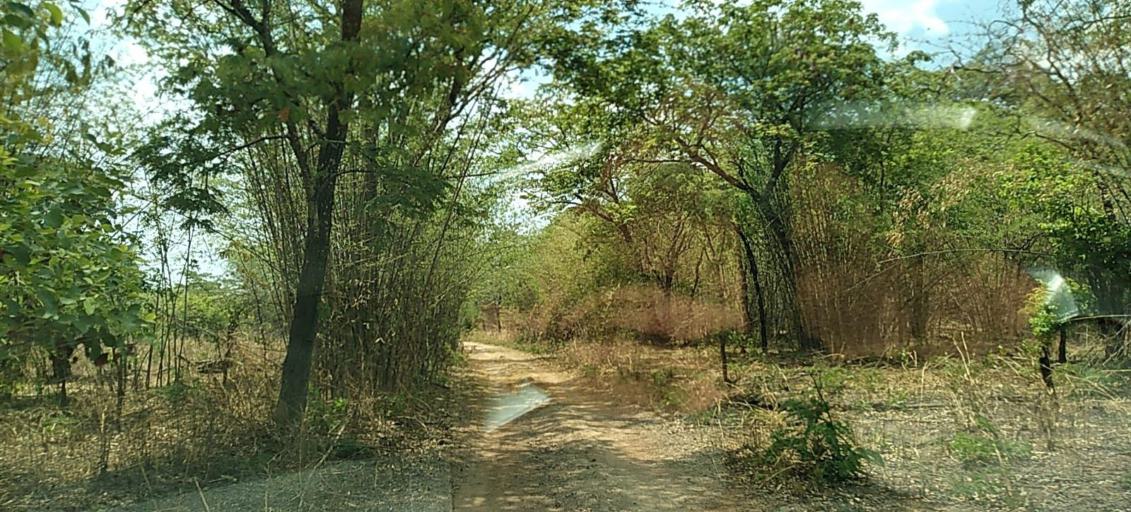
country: ZM
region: Copperbelt
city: Chililabombwe
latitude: -12.4684
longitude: 27.6496
